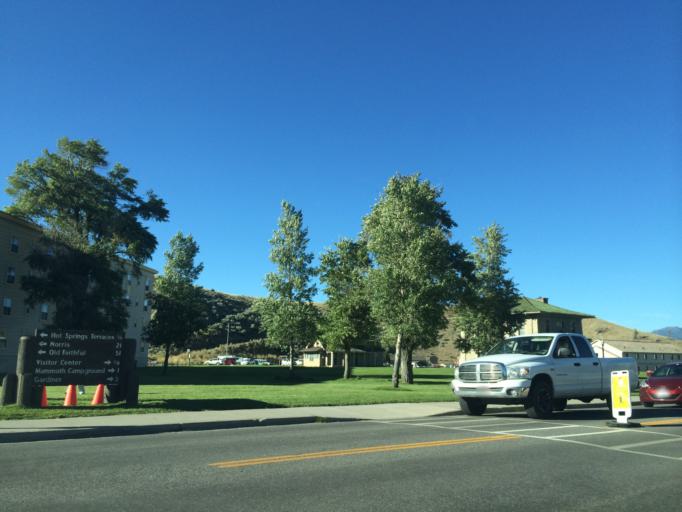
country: US
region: Montana
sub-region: Gallatin County
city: West Yellowstone
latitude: 44.9768
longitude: -110.6999
